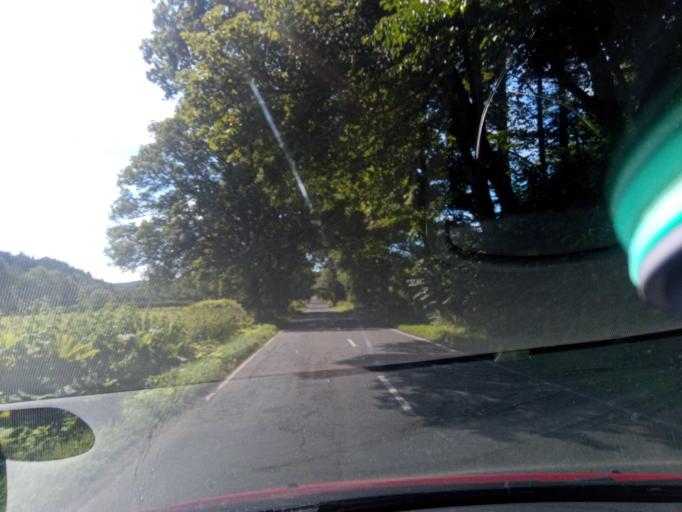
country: GB
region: England
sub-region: Northumberland
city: Bardon Mill
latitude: 54.9156
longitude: -2.3364
